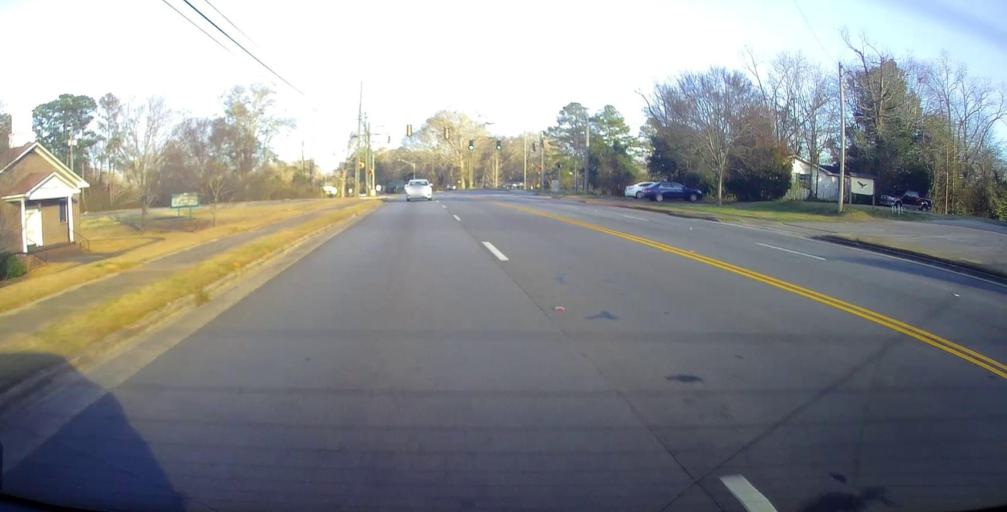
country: US
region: Georgia
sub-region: Troup County
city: West Point
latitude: 32.8753
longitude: -85.1673
